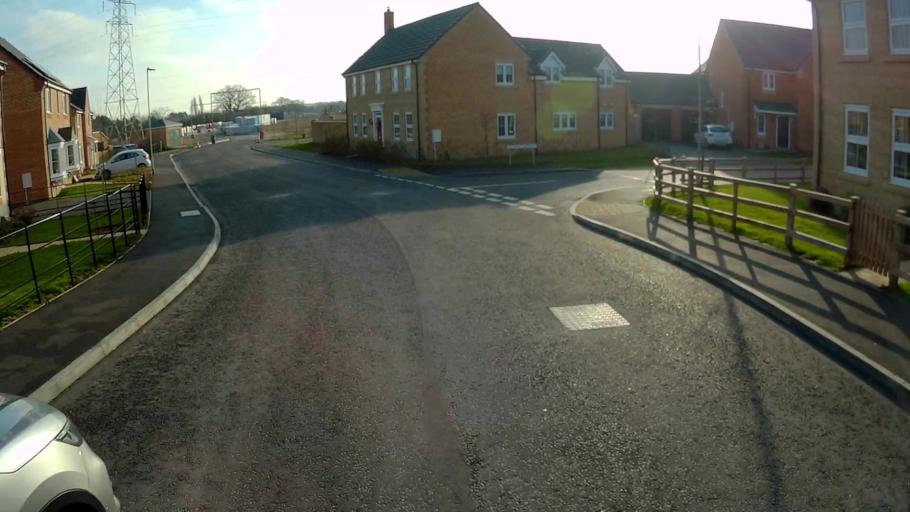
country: GB
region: England
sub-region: Lincolnshire
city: Bourne
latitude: 52.7646
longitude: -0.3938
